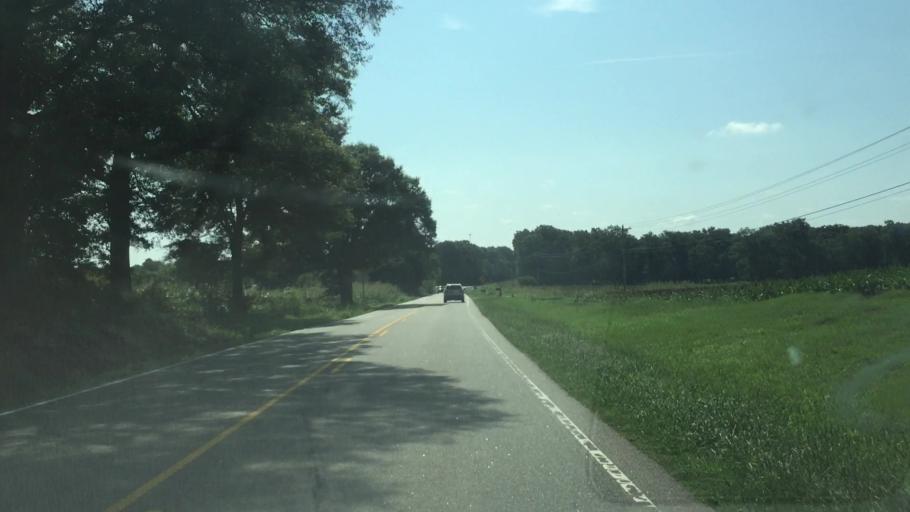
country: US
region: North Carolina
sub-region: Union County
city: Unionville
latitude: 35.1335
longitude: -80.4481
